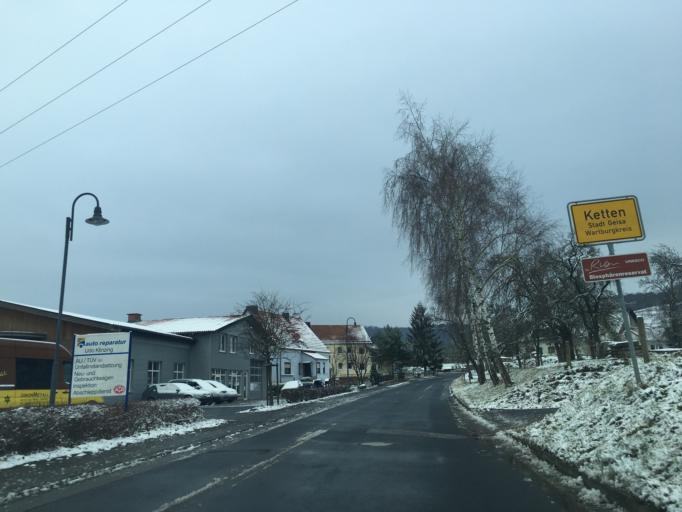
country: DE
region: Thuringia
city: Schleid
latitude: 50.6490
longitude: 9.9296
